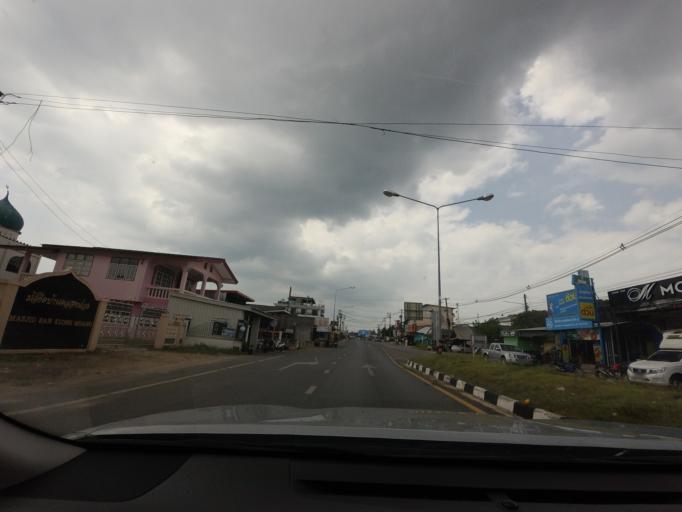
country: TH
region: Phangnga
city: Ban Ao Nang
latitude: 8.0526
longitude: 98.7617
